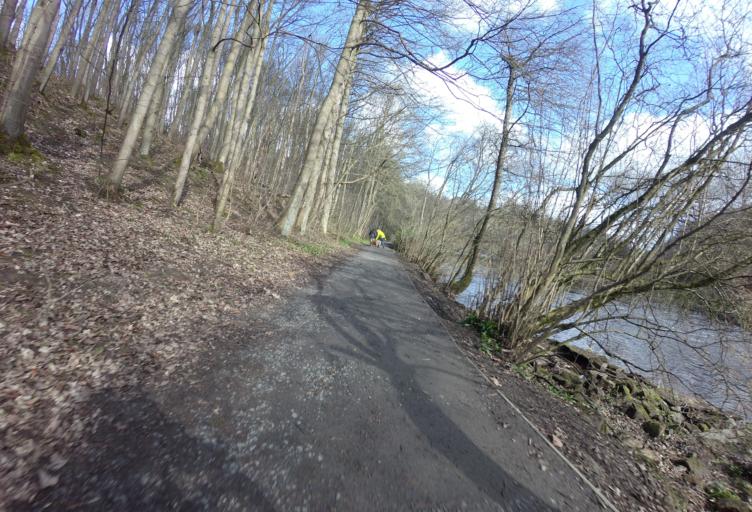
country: GB
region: Scotland
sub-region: West Lothian
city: East Calder
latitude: 55.9016
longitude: -3.4631
